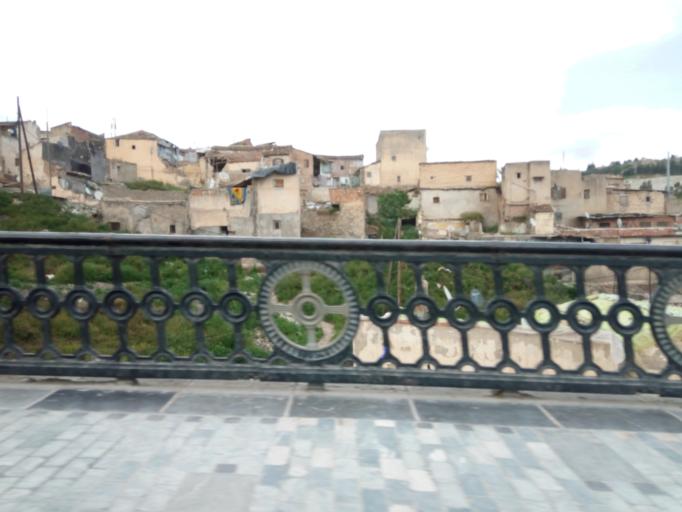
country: DZ
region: Constantine
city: Constantine
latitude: 36.3639
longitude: 6.6119
